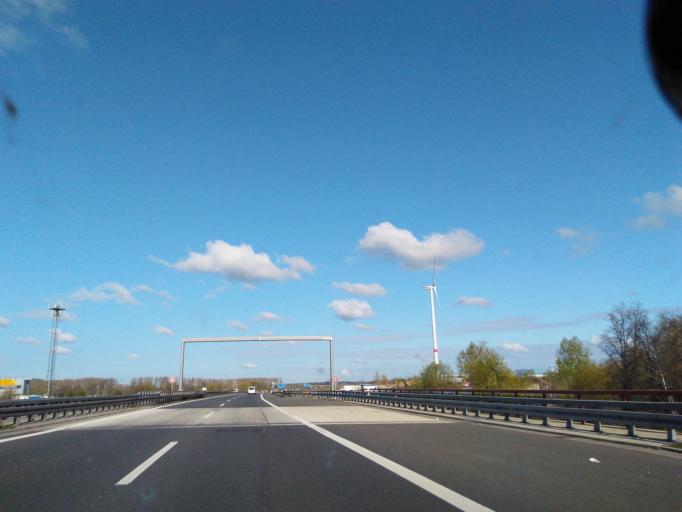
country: DE
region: Berlin
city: Buchholz
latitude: 52.6356
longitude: 13.4415
